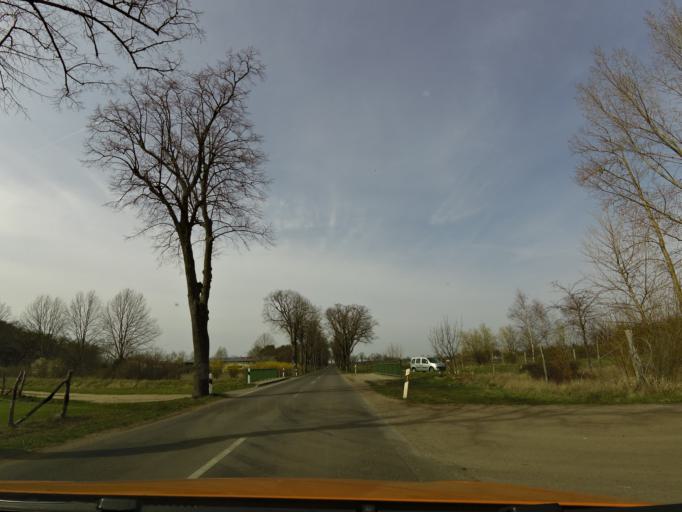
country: DE
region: Brandenburg
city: Stahnsdorf
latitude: 52.3124
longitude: 13.1568
